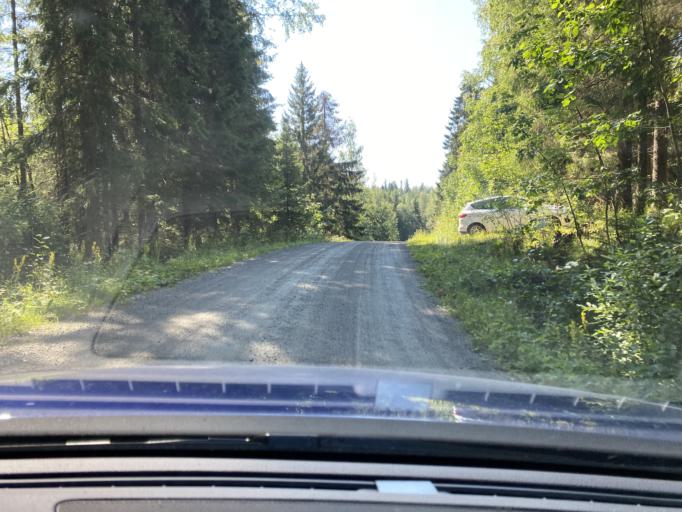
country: FI
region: Central Finland
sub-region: Jaemsae
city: Jaemsae
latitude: 61.8351
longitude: 25.3706
